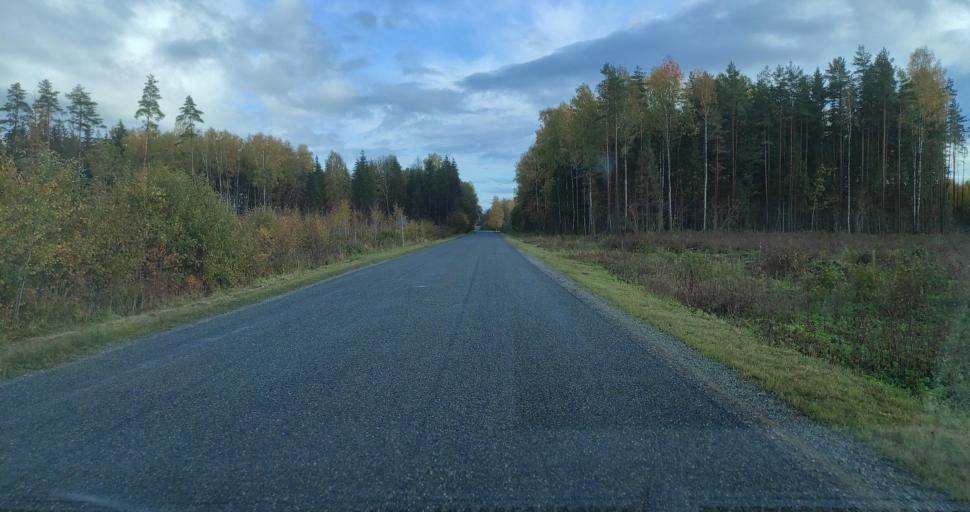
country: LV
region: Skrunda
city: Skrunda
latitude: 56.6055
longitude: 21.9215
